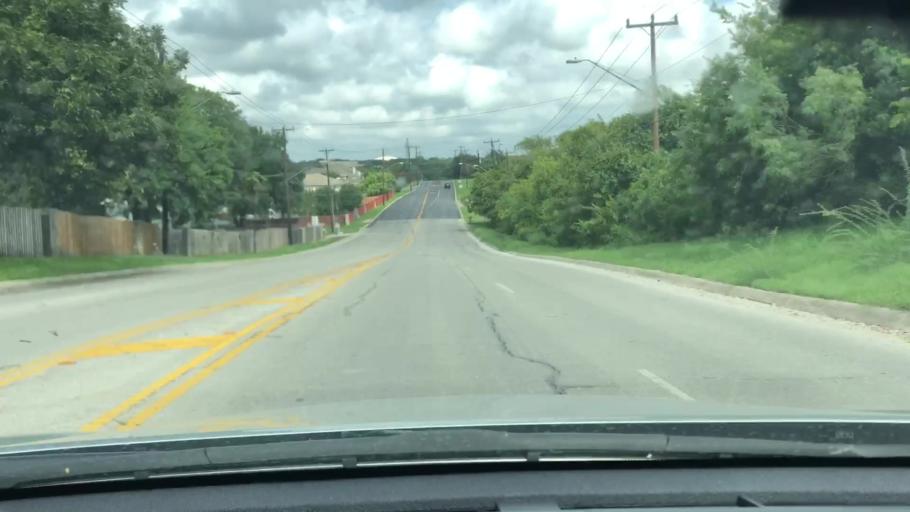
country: US
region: Texas
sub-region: Bexar County
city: Windcrest
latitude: 29.5258
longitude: -98.3693
